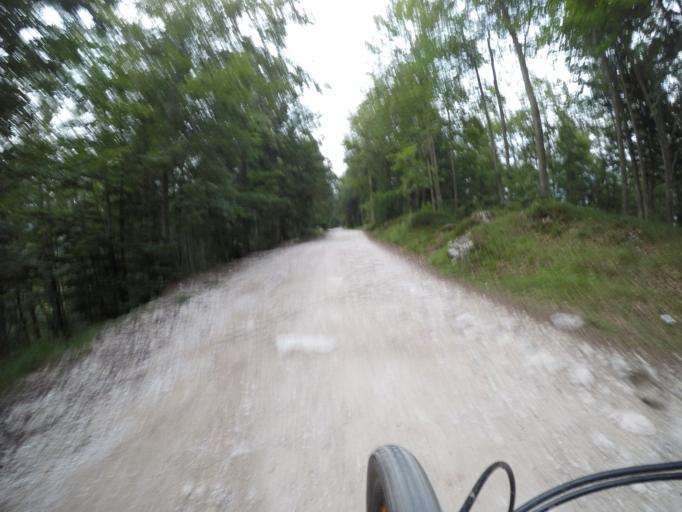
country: IT
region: Veneto
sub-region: Provincia di Vicenza
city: Gallio
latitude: 45.9058
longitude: 11.5249
